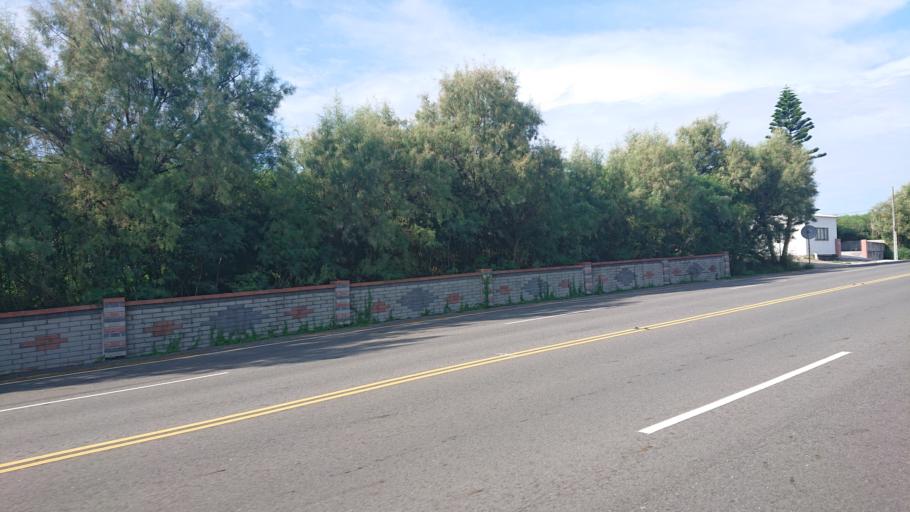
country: TW
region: Taiwan
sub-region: Penghu
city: Ma-kung
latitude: 23.5206
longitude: 119.5813
